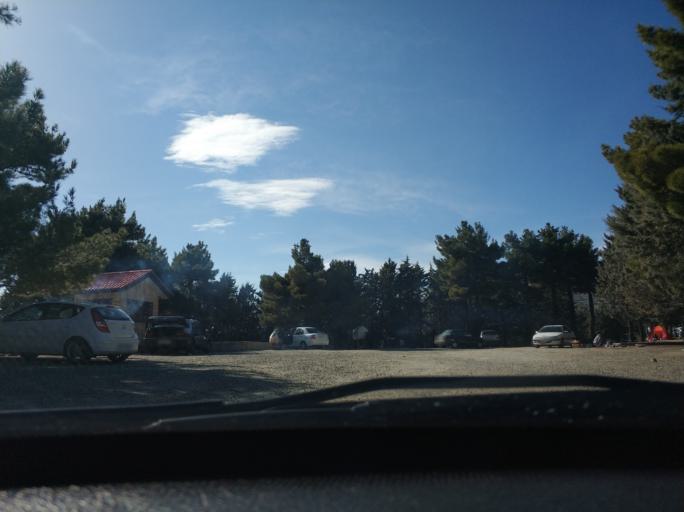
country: IR
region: Tehran
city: Tajrish
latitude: 35.8020
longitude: 51.5671
